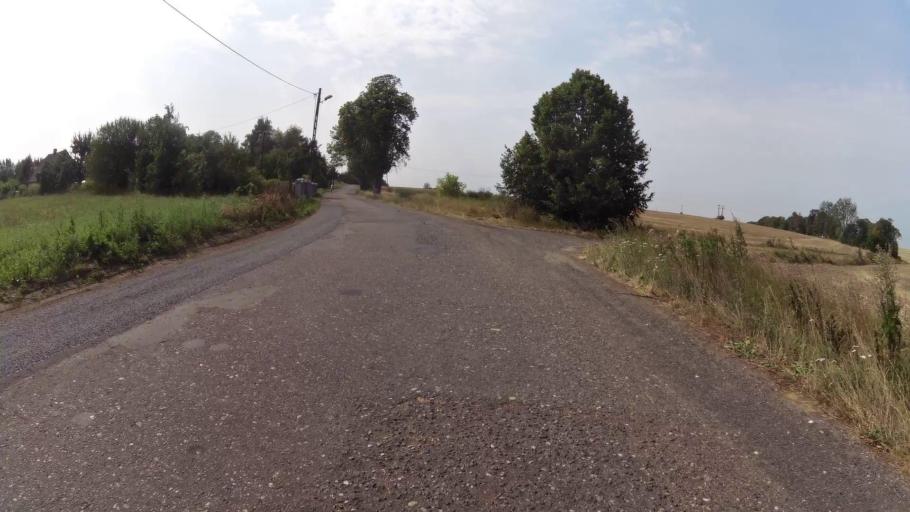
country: PL
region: West Pomeranian Voivodeship
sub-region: Powiat gryfinski
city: Moryn
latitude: 52.8694
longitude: 14.4675
